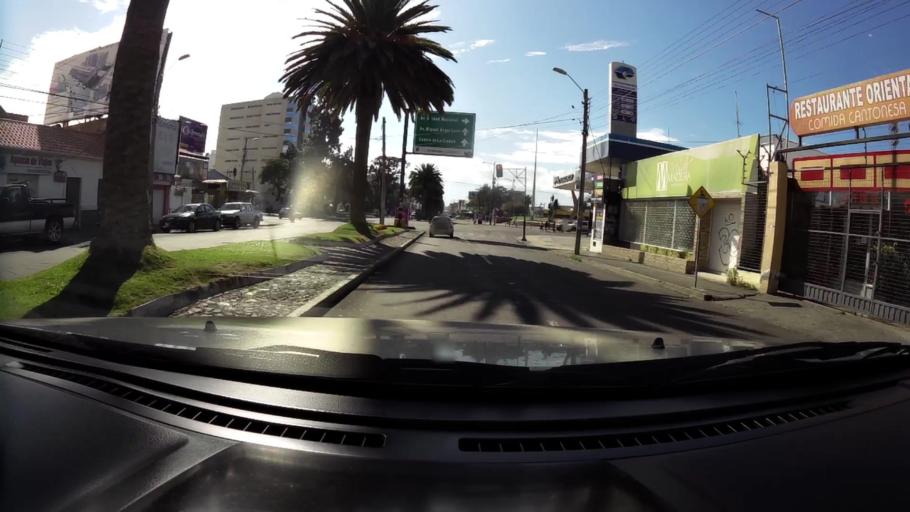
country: EC
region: Chimborazo
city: Riobamba
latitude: -1.6648
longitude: -78.6593
